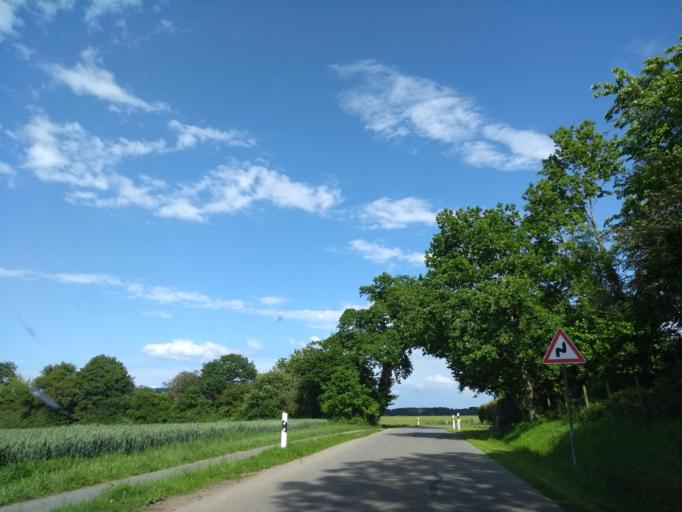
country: DE
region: Schleswig-Holstein
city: Damp
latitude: 54.5670
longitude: 9.9887
